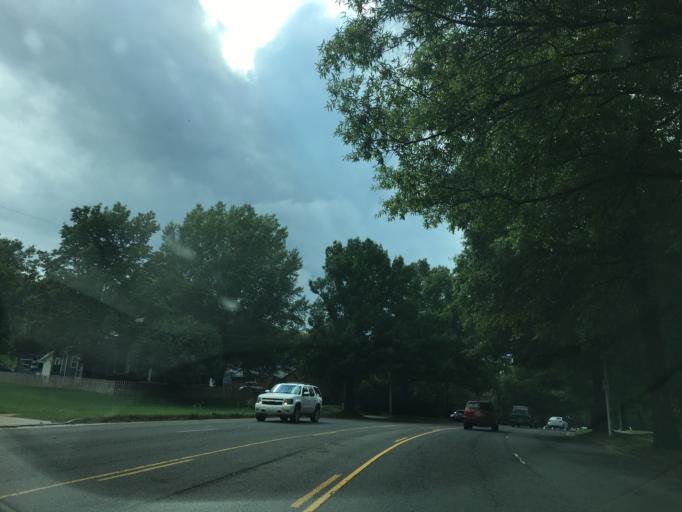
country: US
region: Tennessee
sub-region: Davidson County
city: Nashville
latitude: 36.1390
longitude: -86.8124
